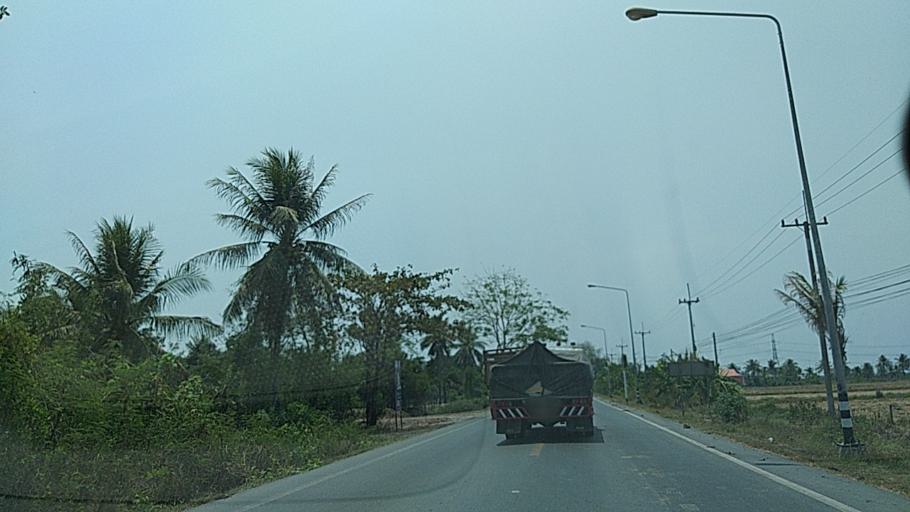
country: TH
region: Chachoengsao
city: Bang Nam Priao
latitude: 13.8987
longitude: 100.9719
